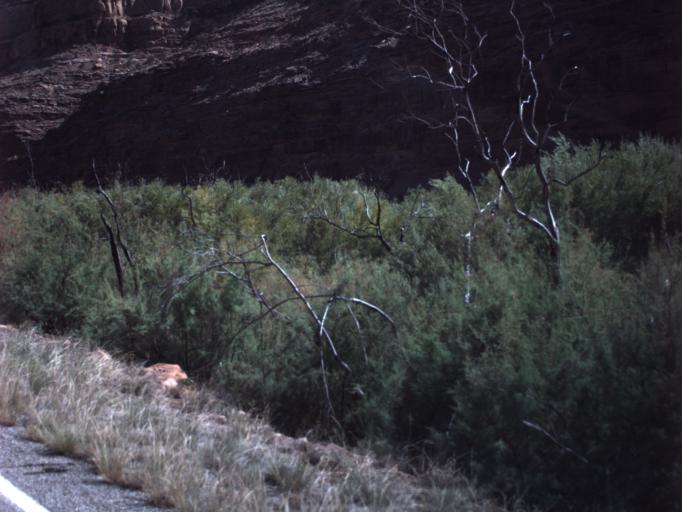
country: US
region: Utah
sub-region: Grand County
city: Moab
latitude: 38.5318
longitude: -109.6198
